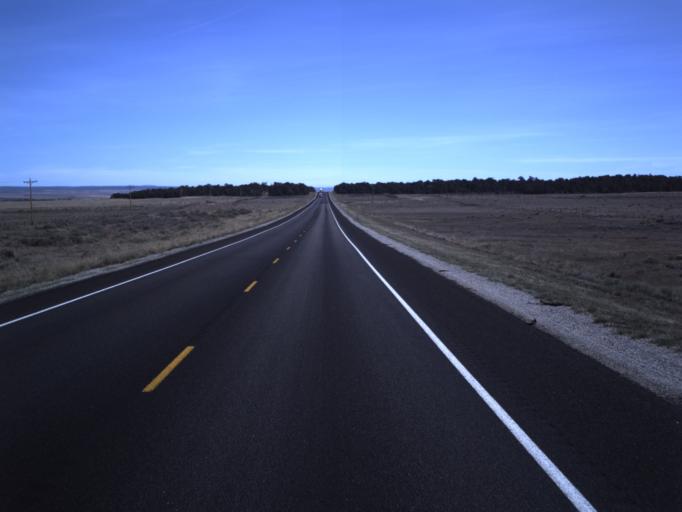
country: US
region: Colorado
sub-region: Dolores County
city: Dove Creek
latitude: 37.8344
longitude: -109.1045
